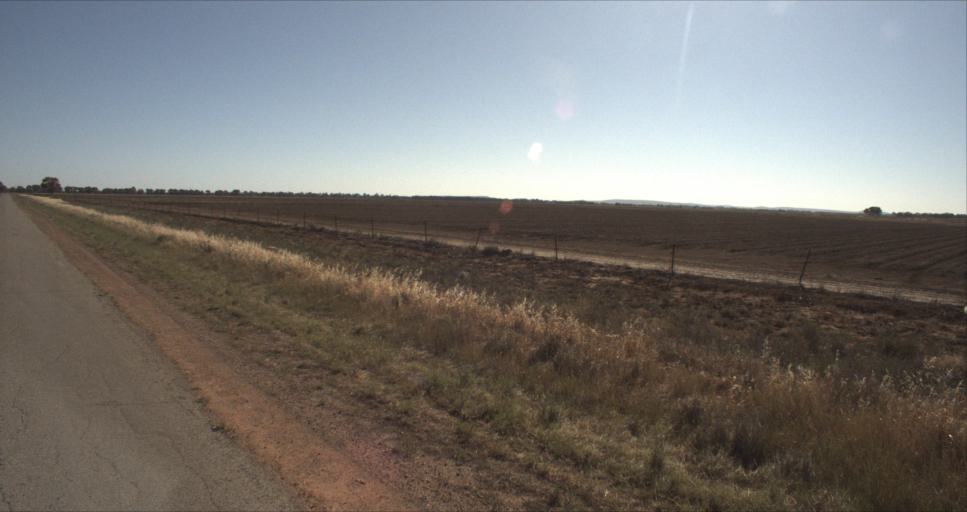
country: AU
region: New South Wales
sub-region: Leeton
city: Leeton
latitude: -34.5655
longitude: 146.3119
